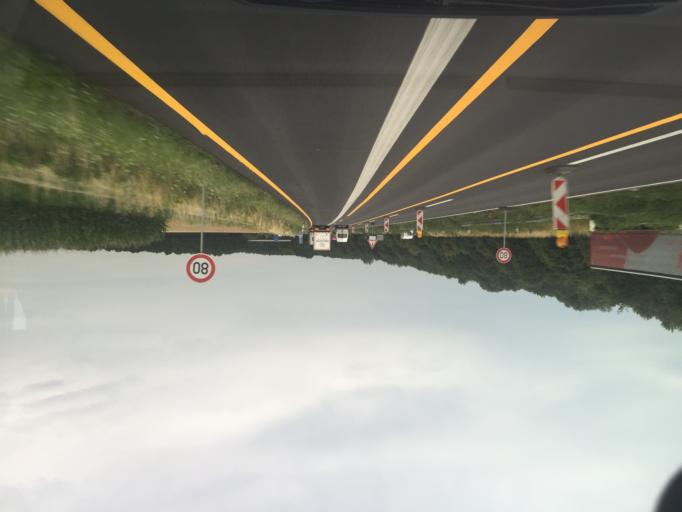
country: DE
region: North Rhine-Westphalia
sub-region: Regierungsbezirk Dusseldorf
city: Viersen
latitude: 51.2757
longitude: 6.3426
